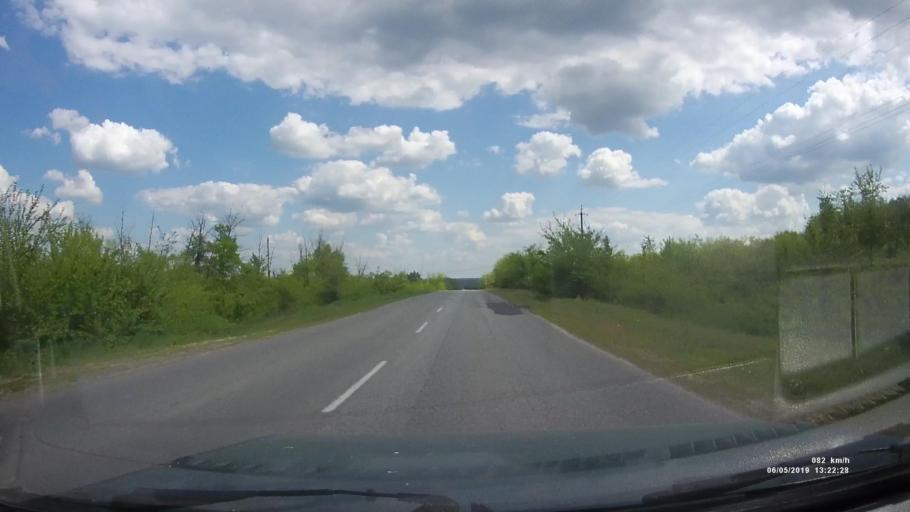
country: RU
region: Rostov
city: Ust'-Donetskiy
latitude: 47.6959
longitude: 40.9204
